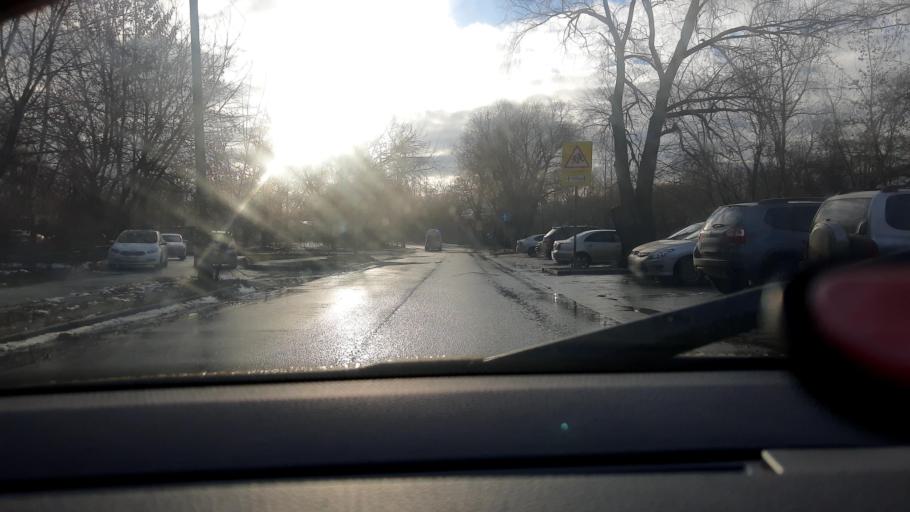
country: RU
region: Moskovskaya
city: Pushkino
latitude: 55.9948
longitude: 37.8614
